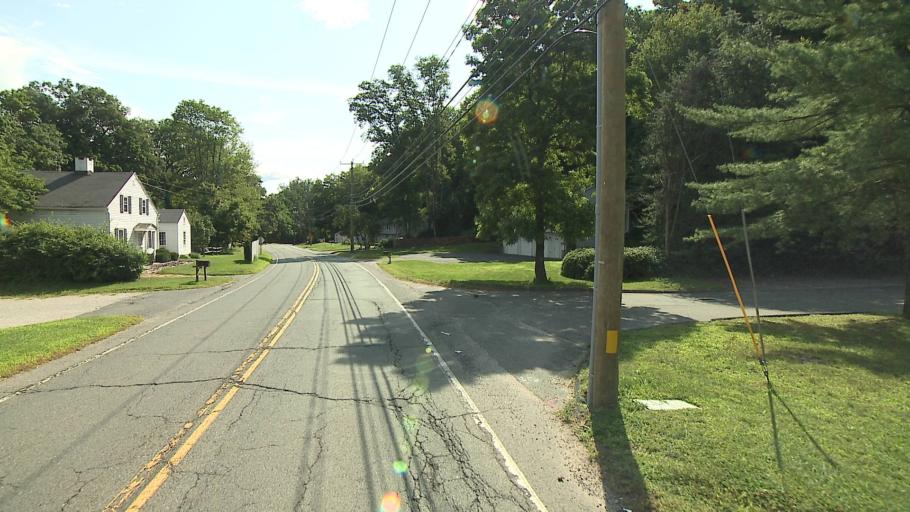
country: US
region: Connecticut
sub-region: Litchfield County
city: New Milford
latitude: 41.5825
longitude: -73.4390
